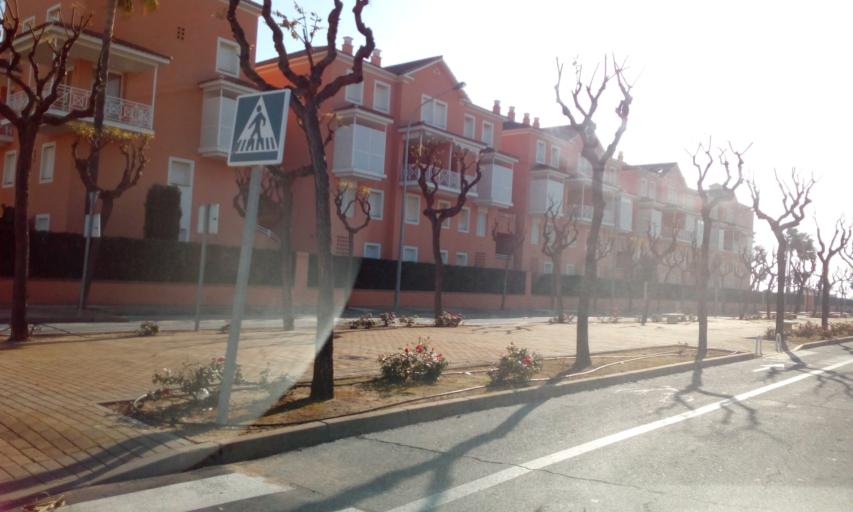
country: ES
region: Andalusia
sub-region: Provincia de Huelva
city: Lepe
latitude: 37.2066
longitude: -7.2344
